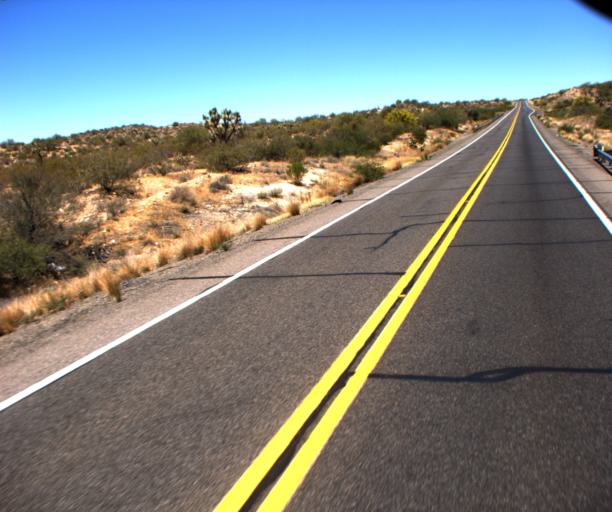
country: US
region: Arizona
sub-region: Yavapai County
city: Congress
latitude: 34.2117
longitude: -113.0659
